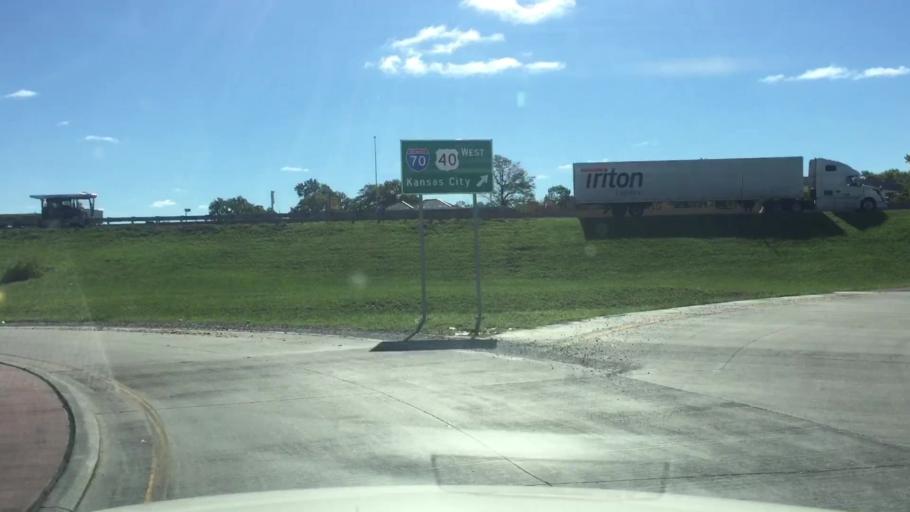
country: US
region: Missouri
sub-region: Boone County
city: Columbia
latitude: 38.9664
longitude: -92.3535
